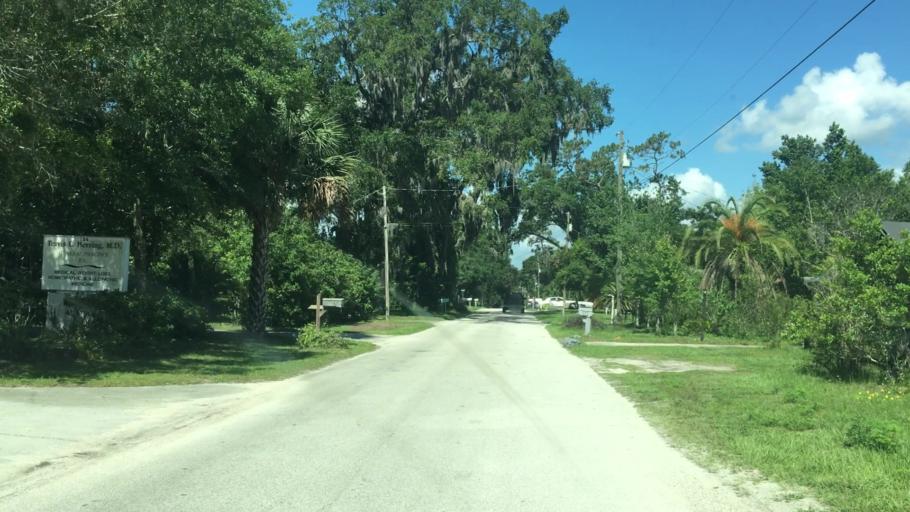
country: US
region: Florida
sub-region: Volusia County
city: Orange City
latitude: 28.9291
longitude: -81.2998
